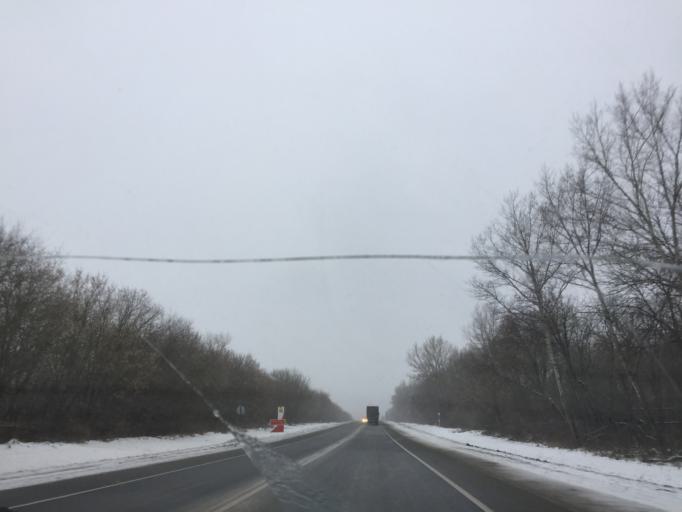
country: RU
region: Tula
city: Plavsk
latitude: 53.7636
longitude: 37.3411
